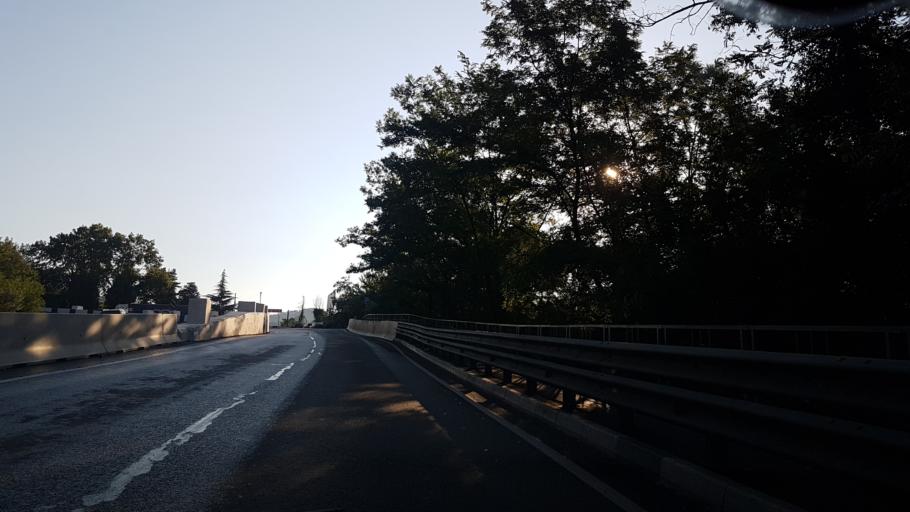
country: RU
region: Krasnodarskiy
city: Dagomys
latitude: 43.6426
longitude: 39.7008
